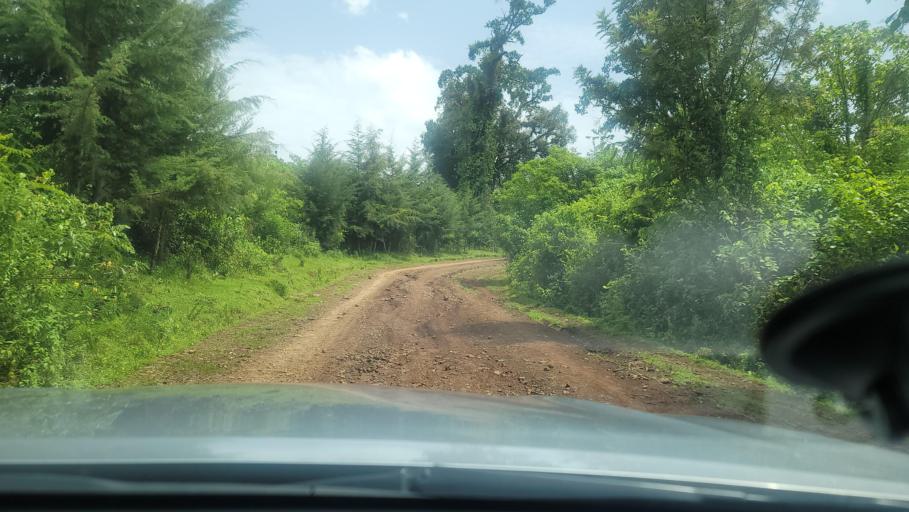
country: ET
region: Oromiya
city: Agaro
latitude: 7.8072
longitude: 36.4135
